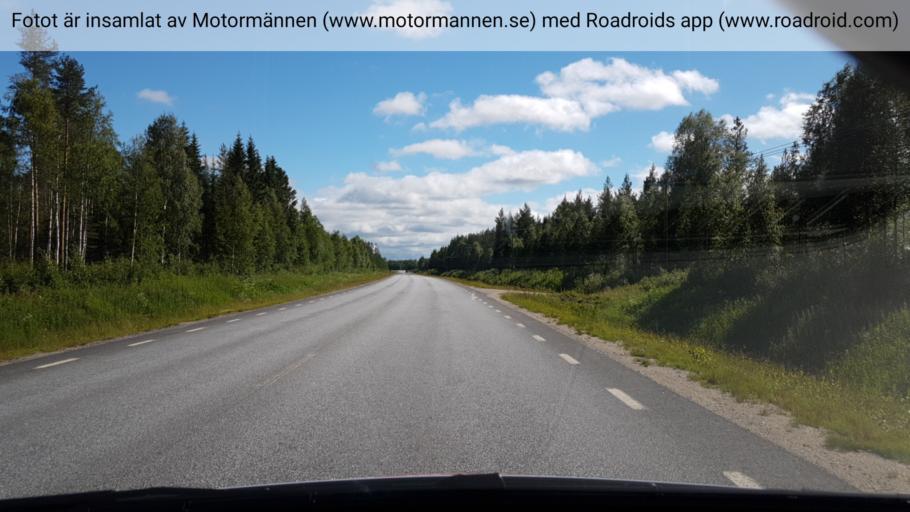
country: SE
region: Vaesterbotten
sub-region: Vannas Kommun
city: Vaennaes
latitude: 64.0207
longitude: 19.6920
